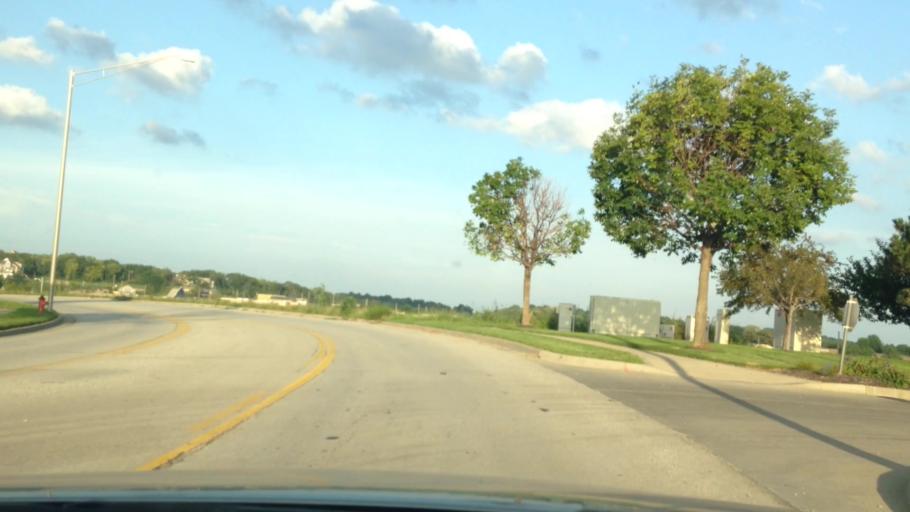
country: US
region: Missouri
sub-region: Clay County
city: Liberty
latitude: 39.2460
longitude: -94.4565
